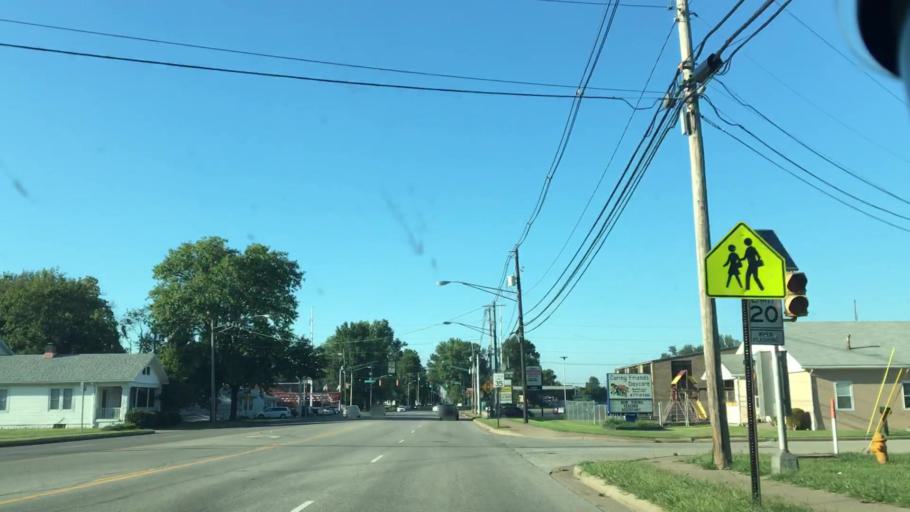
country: US
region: Indiana
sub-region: Vanderburgh County
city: Evansville
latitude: 37.9460
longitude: -87.4929
